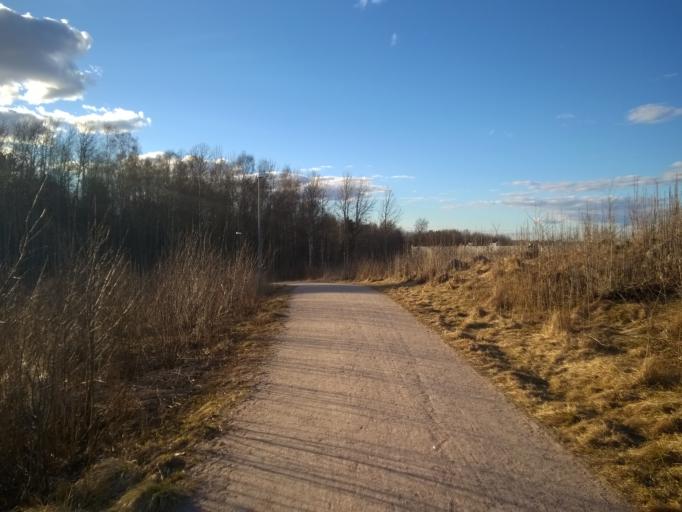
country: FI
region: Uusimaa
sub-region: Helsinki
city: Vantaa
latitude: 60.2467
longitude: 25.0399
